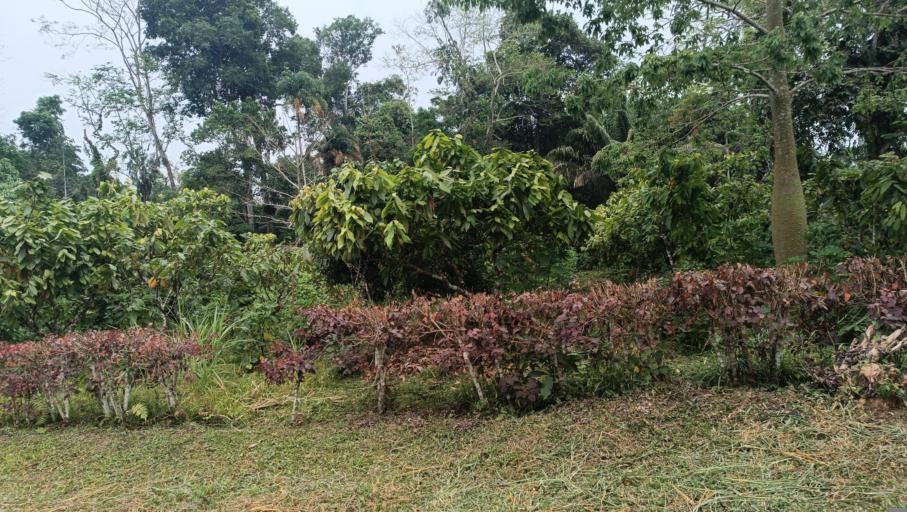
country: BO
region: La Paz
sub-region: Provincia Larecaja
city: Guanay
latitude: -15.5626
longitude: -67.3214
